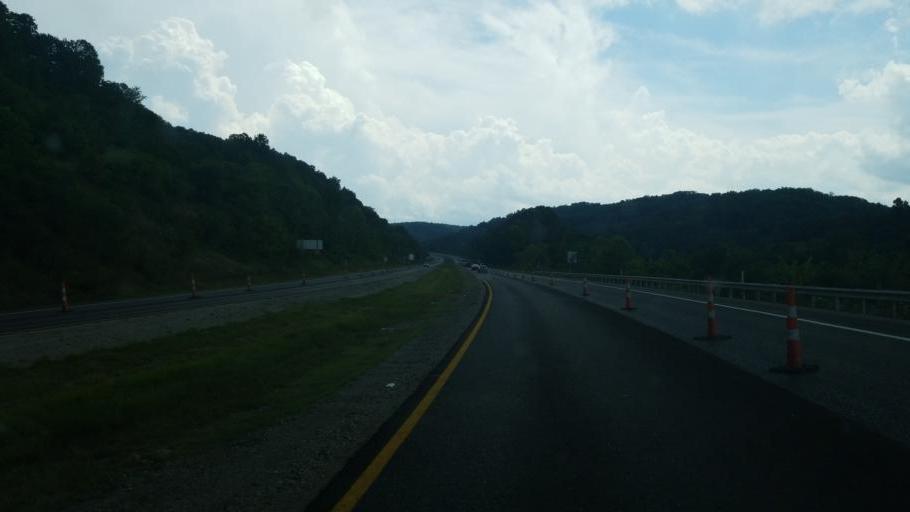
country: US
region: West Virginia
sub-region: Kanawha County
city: Alum Creek
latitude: 38.2638
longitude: -81.8325
